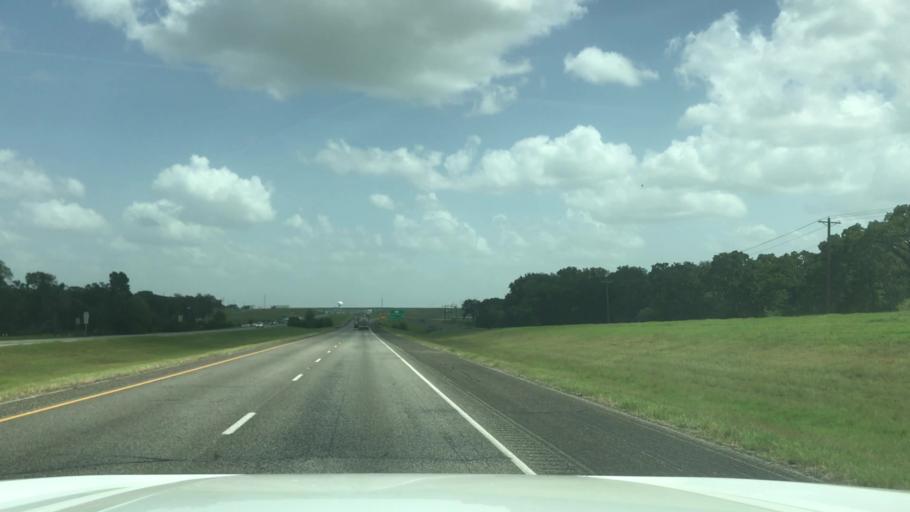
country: US
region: Texas
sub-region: Brazos County
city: Bryan
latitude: 30.7339
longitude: -96.4344
